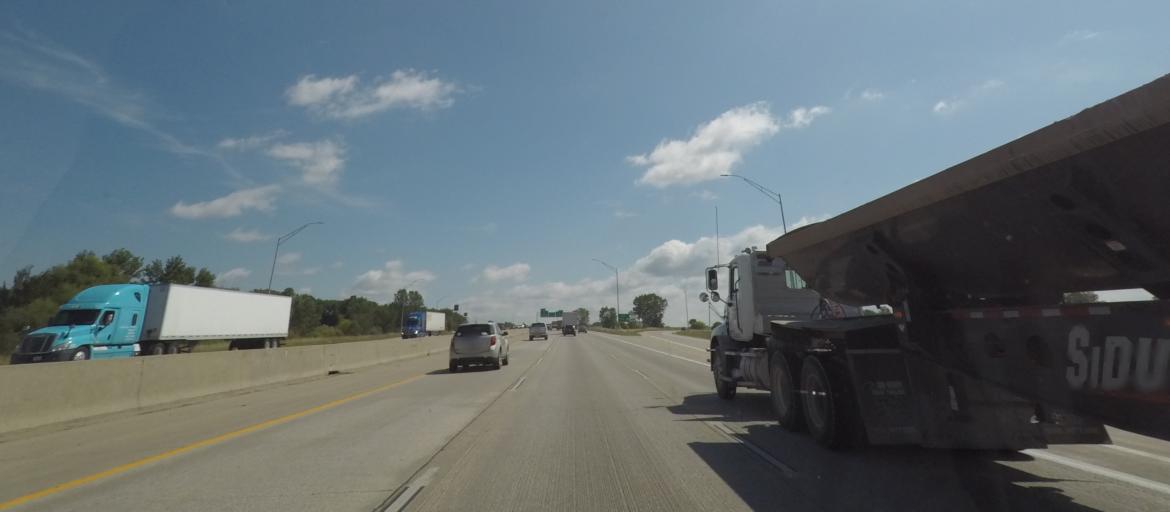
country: US
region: Iowa
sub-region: Polk County
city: Saylorville
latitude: 41.6490
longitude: -93.6082
